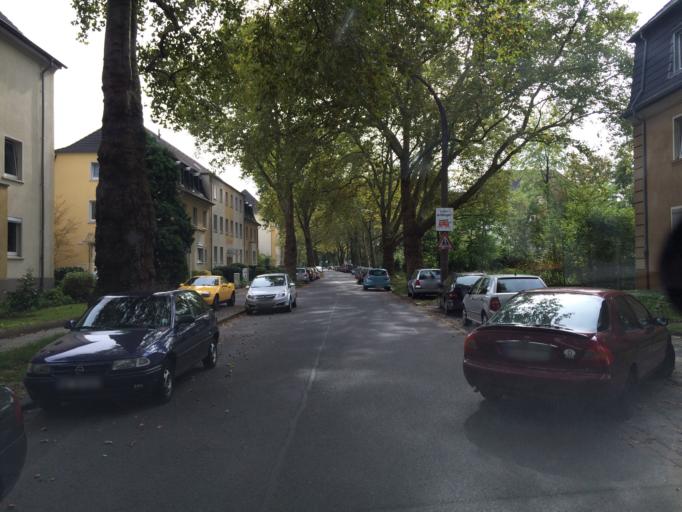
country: DE
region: North Rhine-Westphalia
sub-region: Regierungsbezirk Arnsberg
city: Dortmund
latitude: 51.4849
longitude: 7.4905
